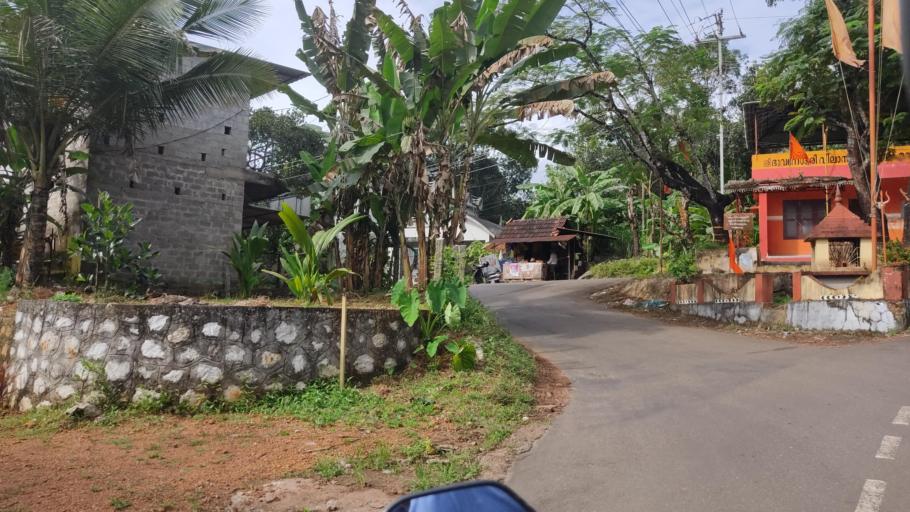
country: IN
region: Kerala
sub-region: Pattanamtitta
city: Adur
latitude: 9.1957
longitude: 76.7785
